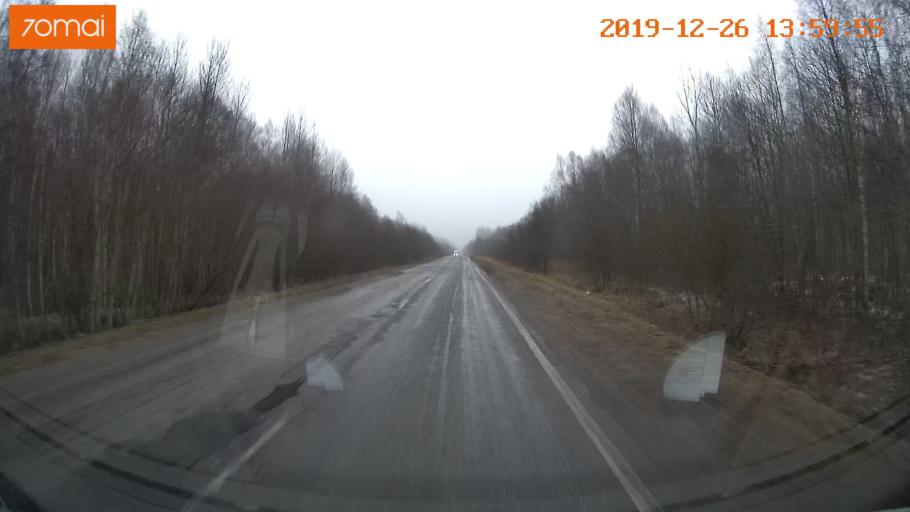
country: RU
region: Jaroslavl
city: Poshekhon'ye
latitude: 58.5619
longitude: 38.7334
